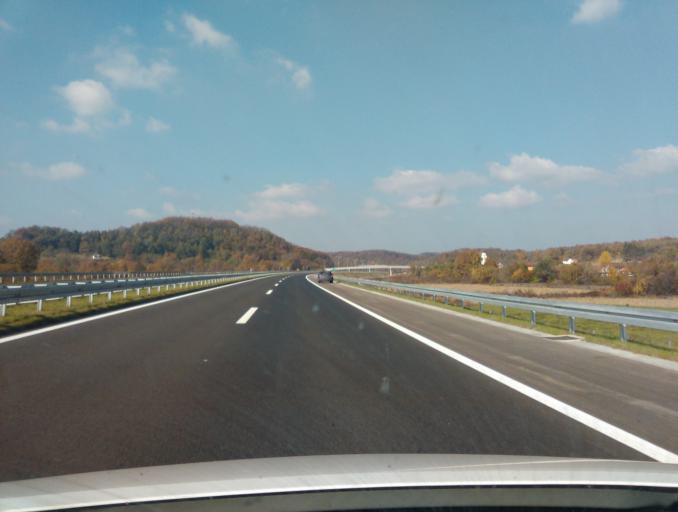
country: BA
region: Republika Srpska
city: Prnjavor
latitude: 44.8867
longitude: 17.6136
